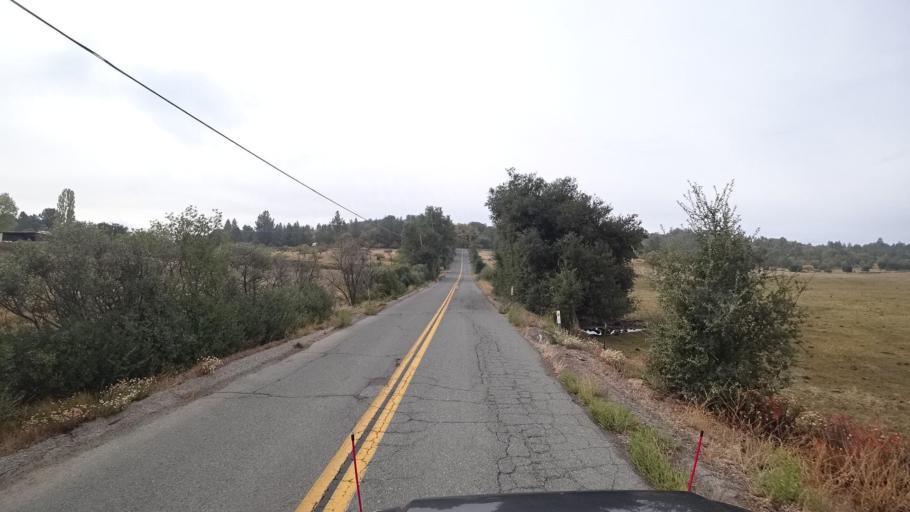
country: US
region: California
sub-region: San Diego County
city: Julian
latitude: 33.0451
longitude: -116.6013
